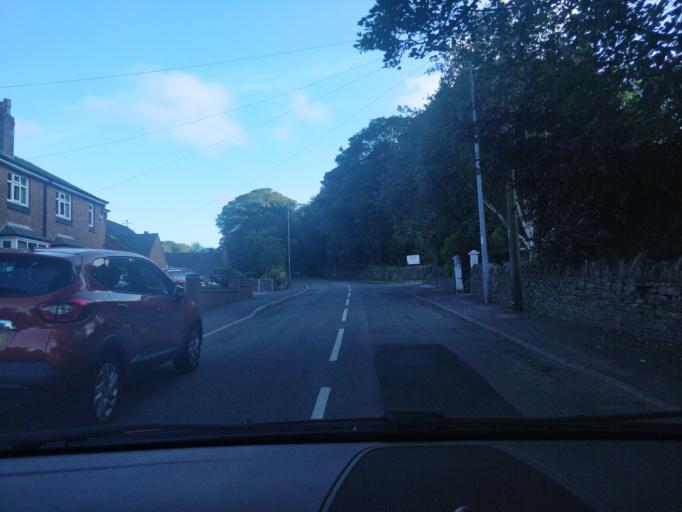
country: GB
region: England
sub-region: St. Helens
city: Billinge
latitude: 53.5184
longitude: -2.7155
